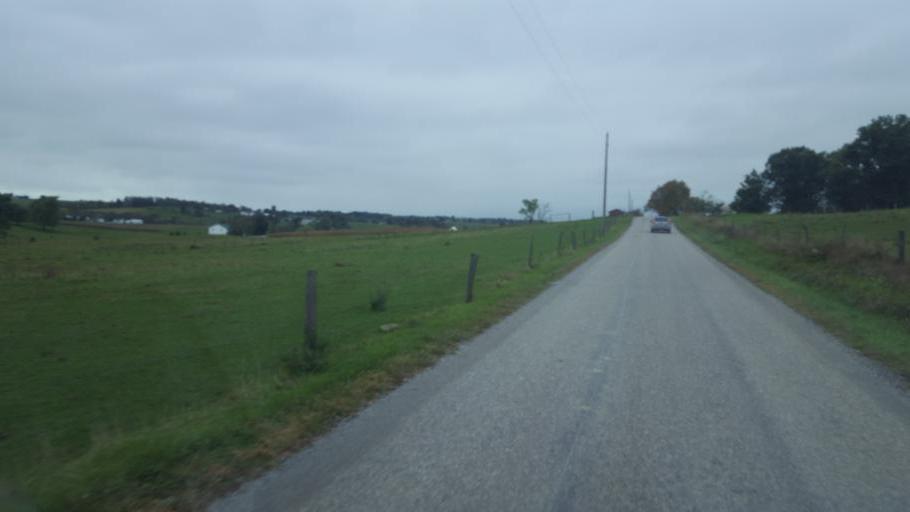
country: US
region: Ohio
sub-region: Wayne County
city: Apple Creek
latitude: 40.6533
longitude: -81.7917
